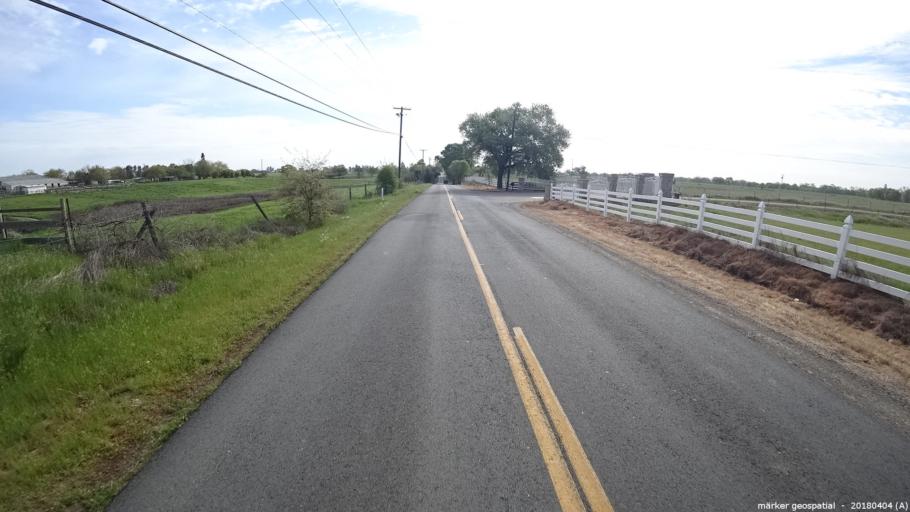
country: US
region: California
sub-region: Sacramento County
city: Herald
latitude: 38.2553
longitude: -121.2563
